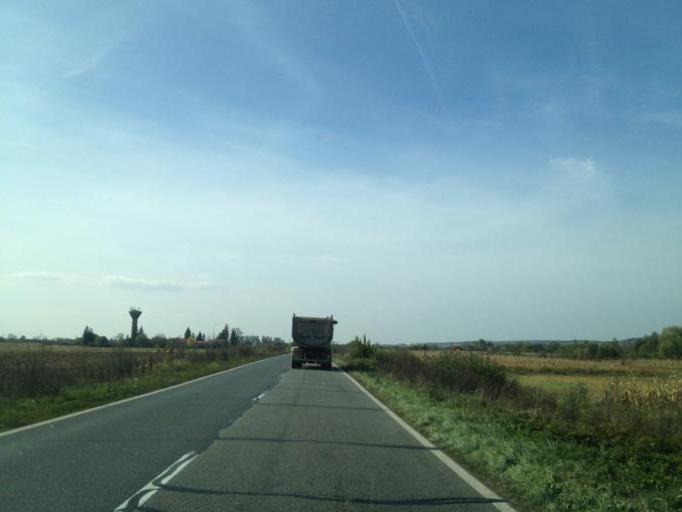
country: RO
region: Timis
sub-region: Comuna Faget
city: Faget
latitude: 45.8585
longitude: 22.2015
